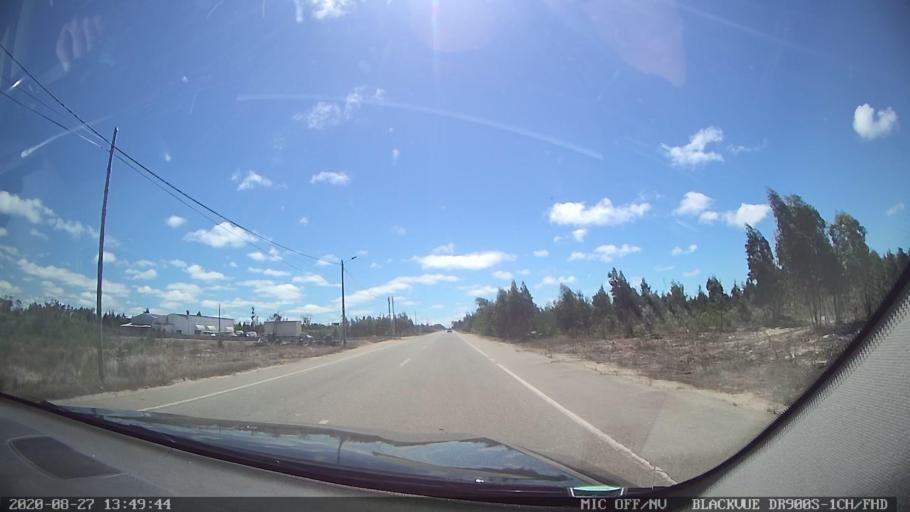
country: PT
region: Coimbra
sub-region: Mira
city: Mira
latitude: 40.3646
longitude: -8.7467
